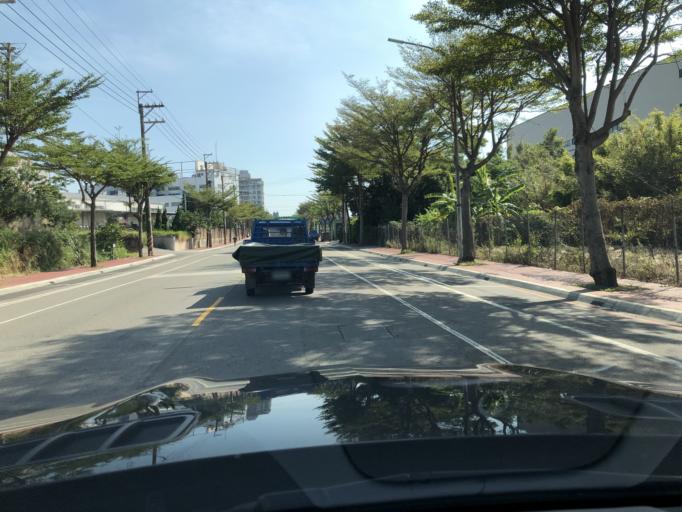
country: TW
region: Taiwan
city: Taoyuan City
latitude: 25.0702
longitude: 121.2889
